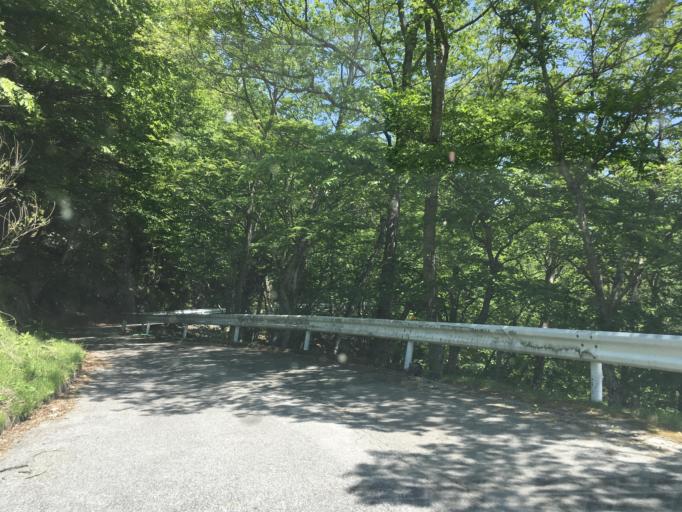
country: JP
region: Iwate
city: Ofunato
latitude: 39.1770
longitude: 141.7286
